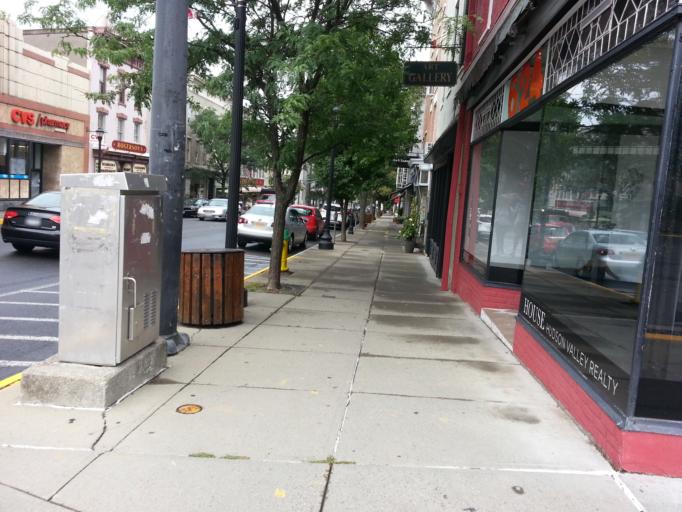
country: US
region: New York
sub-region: Columbia County
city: Oakdale
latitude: 42.2474
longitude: -73.7836
